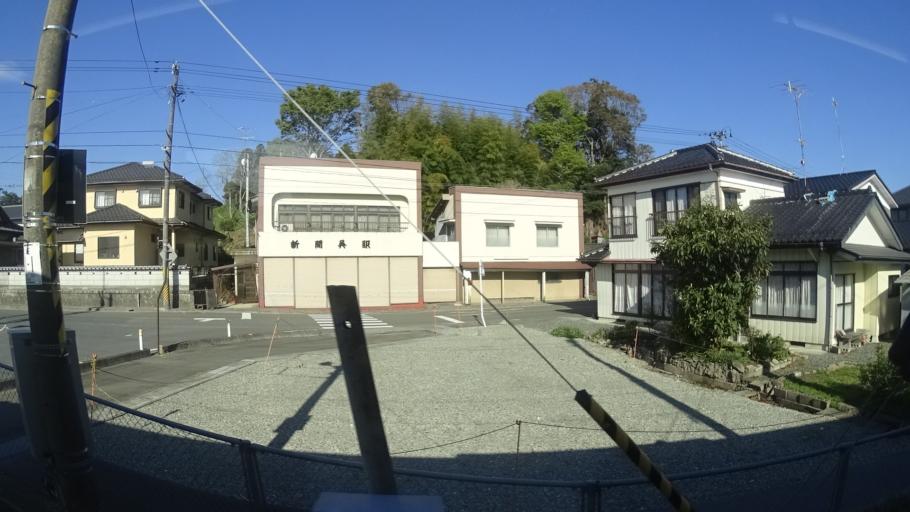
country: JP
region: Fukushima
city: Namie
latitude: 37.5578
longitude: 140.9956
